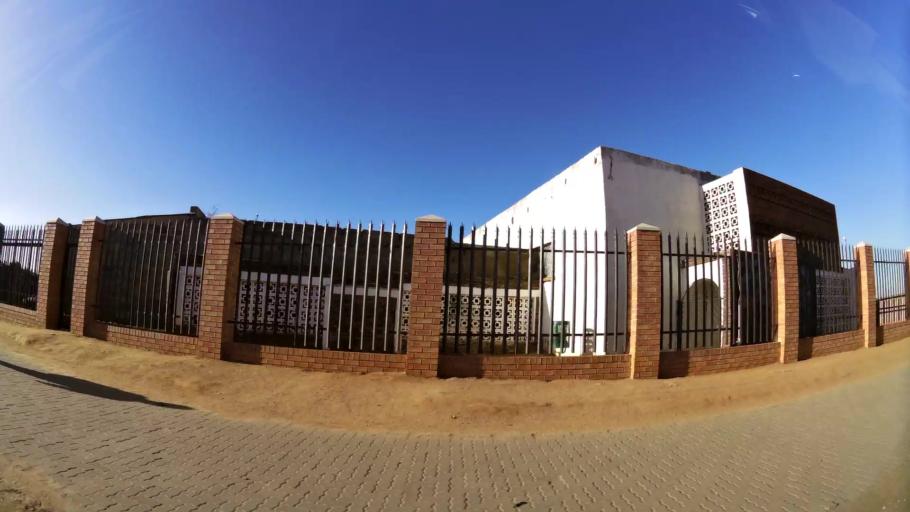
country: ZA
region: Gauteng
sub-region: Ekurhuleni Metropolitan Municipality
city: Tembisa
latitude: -26.0072
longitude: 28.2304
